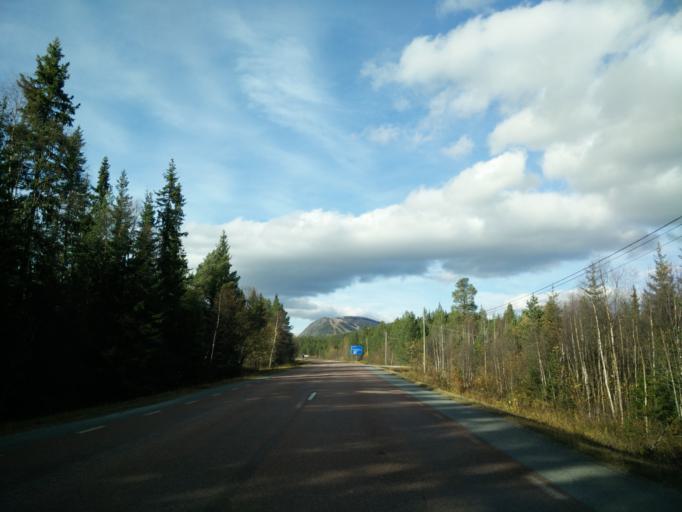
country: NO
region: Hedmark
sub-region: Engerdal
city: Engerdal
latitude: 62.5202
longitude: 12.5947
